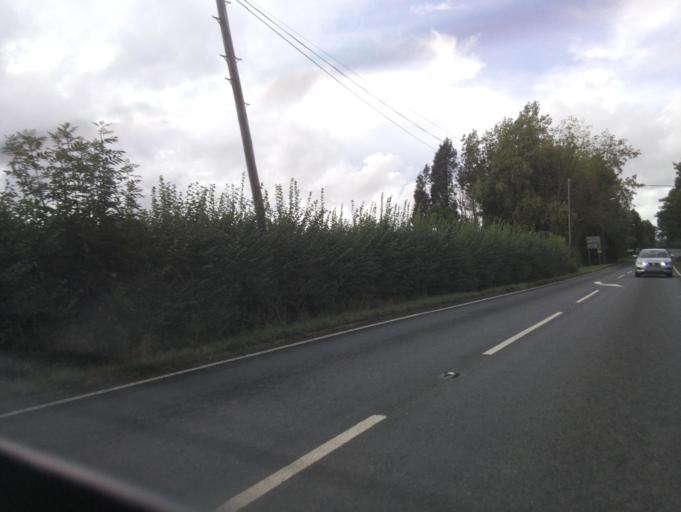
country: GB
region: England
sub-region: Worcestershire
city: Droitwich
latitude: 52.3344
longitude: -2.1820
